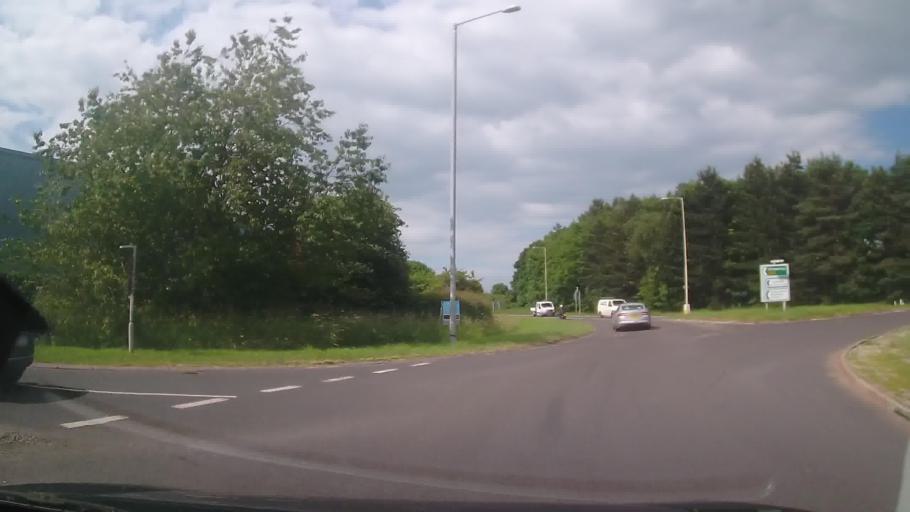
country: GB
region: England
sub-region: Shropshire
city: Ludlow
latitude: 52.3647
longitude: -2.6950
